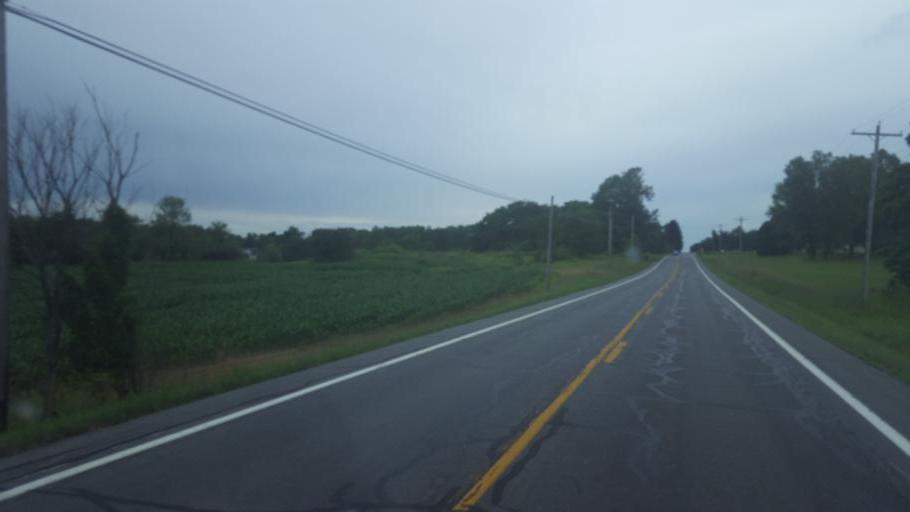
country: US
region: Ohio
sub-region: Richland County
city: Lexington
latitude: 40.6586
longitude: -82.6122
